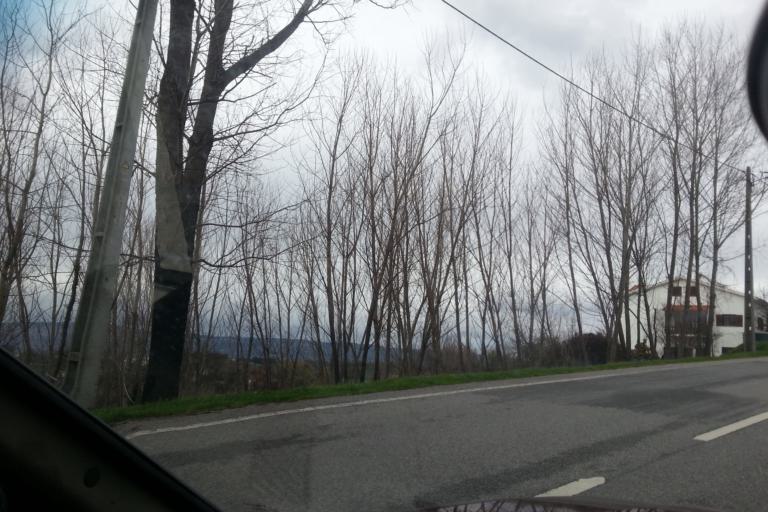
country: PT
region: Guarda
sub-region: Manteigas
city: Manteigas
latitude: 40.4974
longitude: -7.5971
